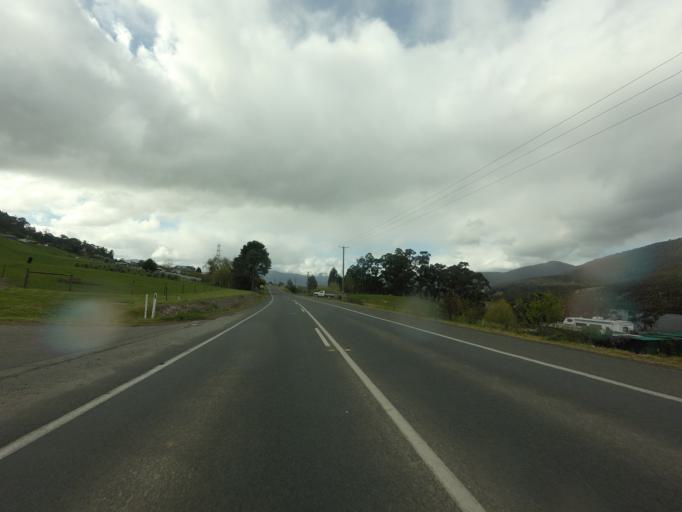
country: AU
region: Tasmania
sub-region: Huon Valley
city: Huonville
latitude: -43.0432
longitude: 147.0440
